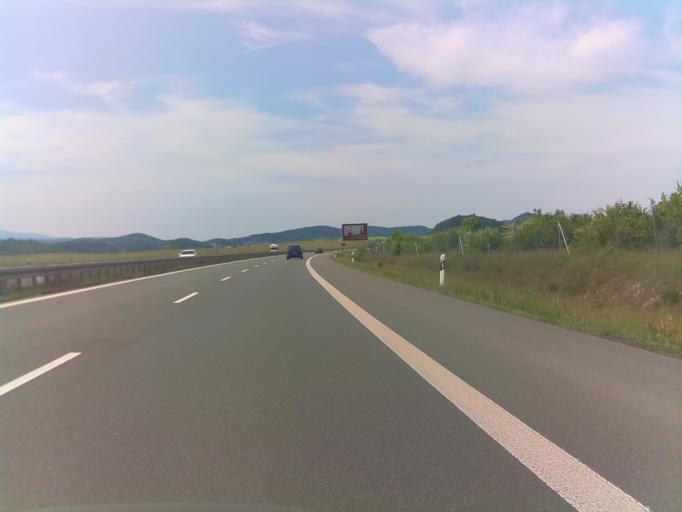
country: DE
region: Saxony-Anhalt
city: Westerhausen
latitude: 51.8121
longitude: 11.1051
